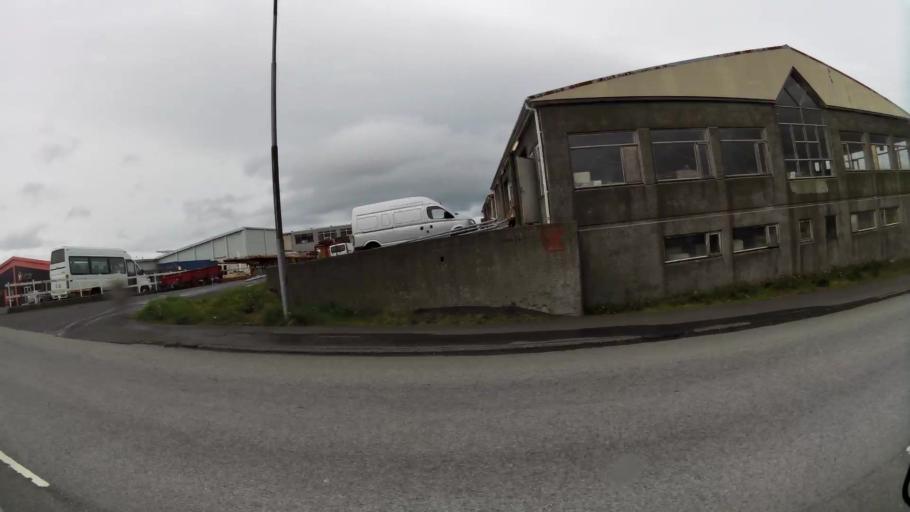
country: IS
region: Capital Region
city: Hafnarfjoerdur
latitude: 64.0624
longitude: -21.9655
